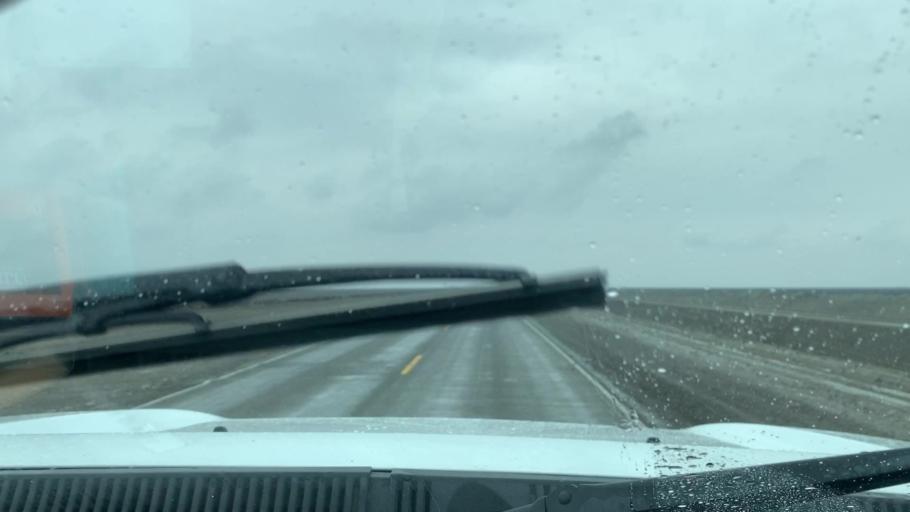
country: US
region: California
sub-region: Tulare County
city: Alpaugh
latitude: 35.9343
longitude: -119.5957
